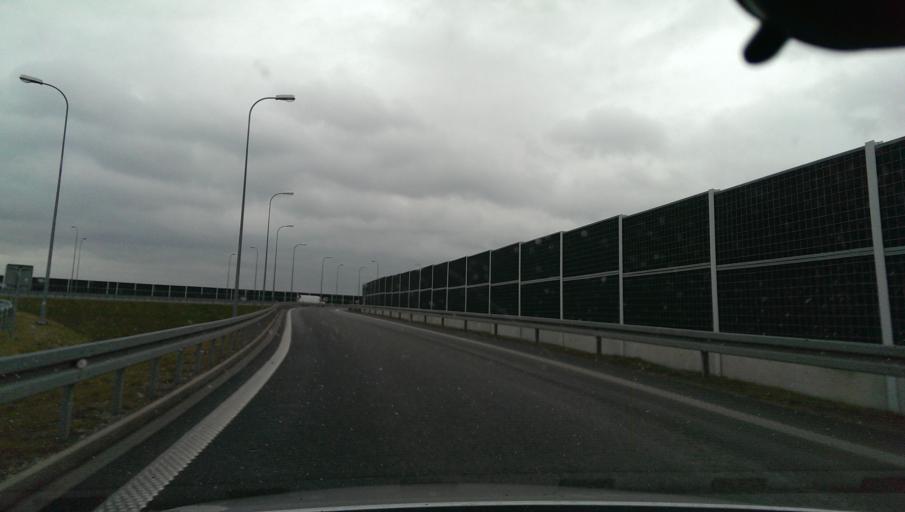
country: PL
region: Lesser Poland Voivodeship
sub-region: Powiat tarnowski
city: Wierzchoslawice
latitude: 50.0145
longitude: 20.8662
